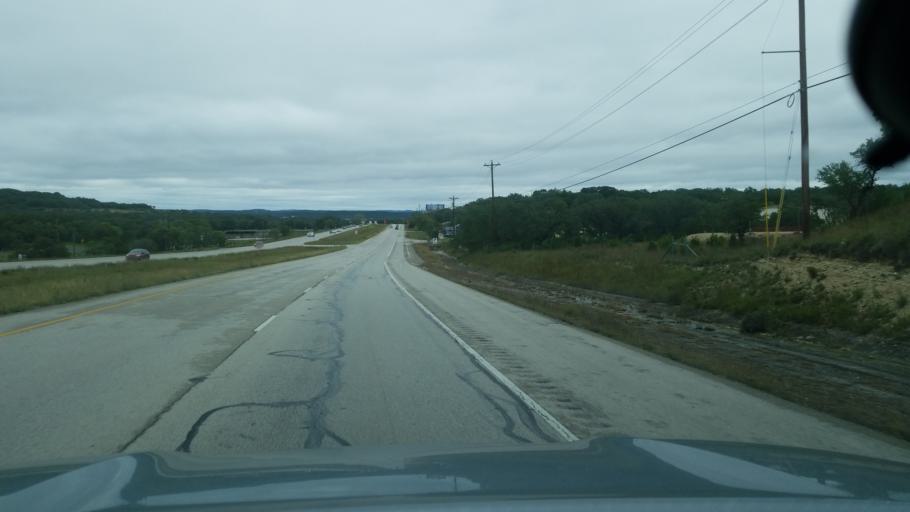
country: US
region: Texas
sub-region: Comal County
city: Bulverde
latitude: 29.8269
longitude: -98.4157
